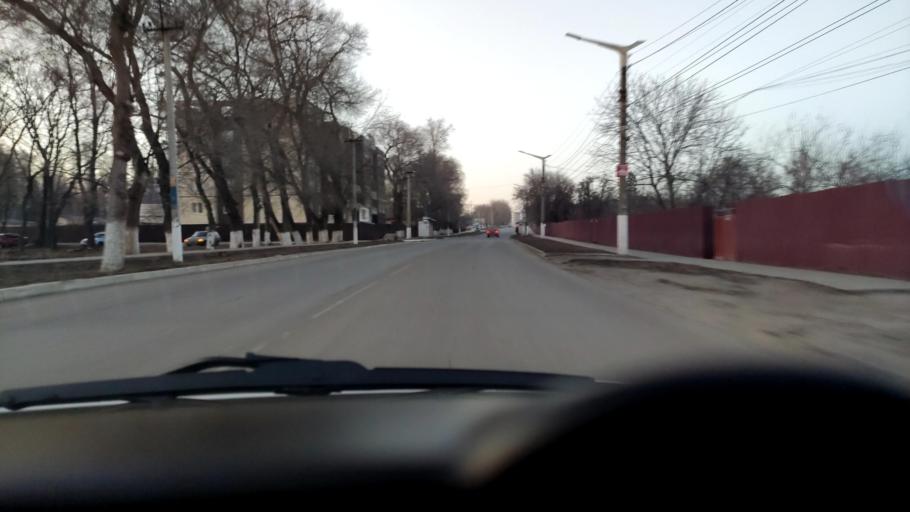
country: RU
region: Voronezj
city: Semiluki
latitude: 51.6914
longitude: 39.0355
